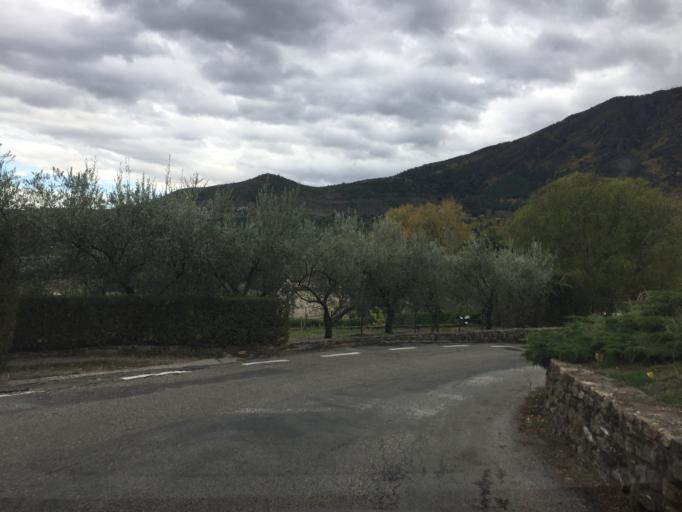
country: FR
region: Rhone-Alpes
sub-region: Departement de l'Ardeche
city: Les Vans
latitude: 44.4212
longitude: 4.0918
